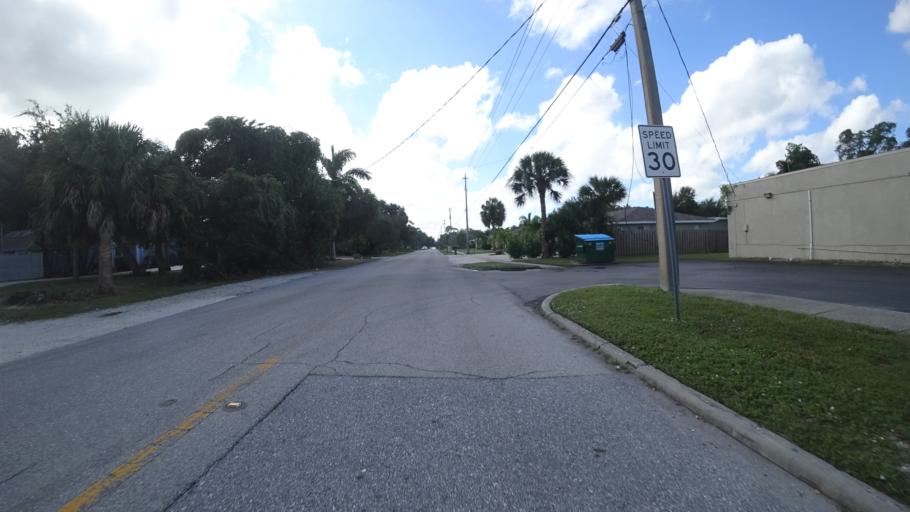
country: US
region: Florida
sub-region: Manatee County
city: West Bradenton
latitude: 27.5119
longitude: -82.6324
